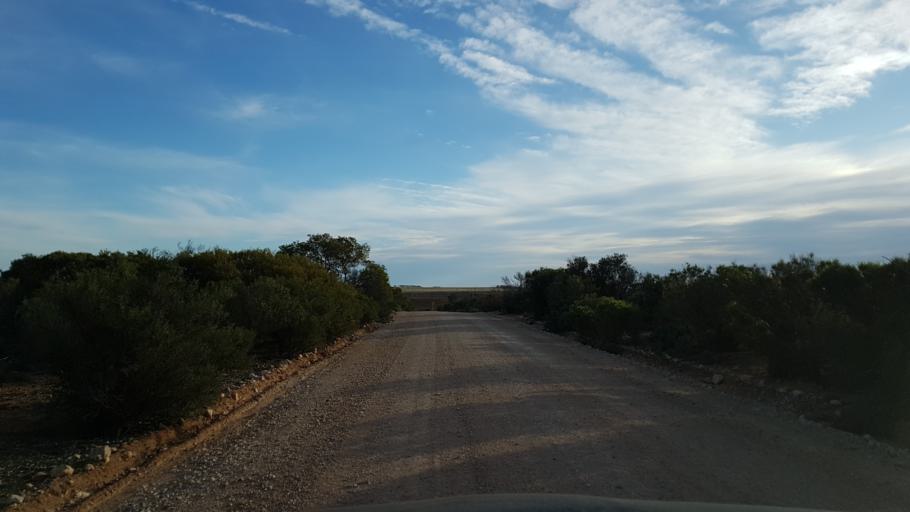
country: AU
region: South Australia
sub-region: Mid Murray
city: Mannum
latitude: -34.7508
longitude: 139.5741
